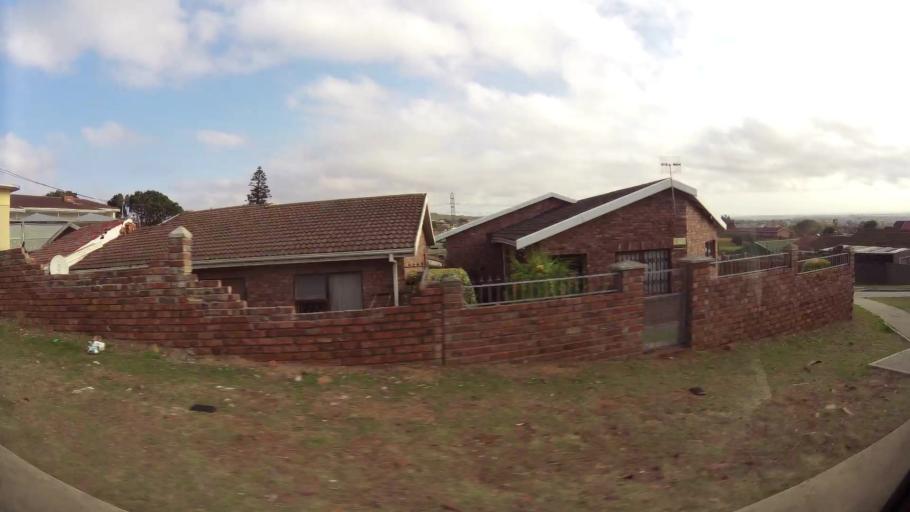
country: ZA
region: Eastern Cape
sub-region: Nelson Mandela Bay Metropolitan Municipality
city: Port Elizabeth
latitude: -33.9232
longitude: 25.5532
